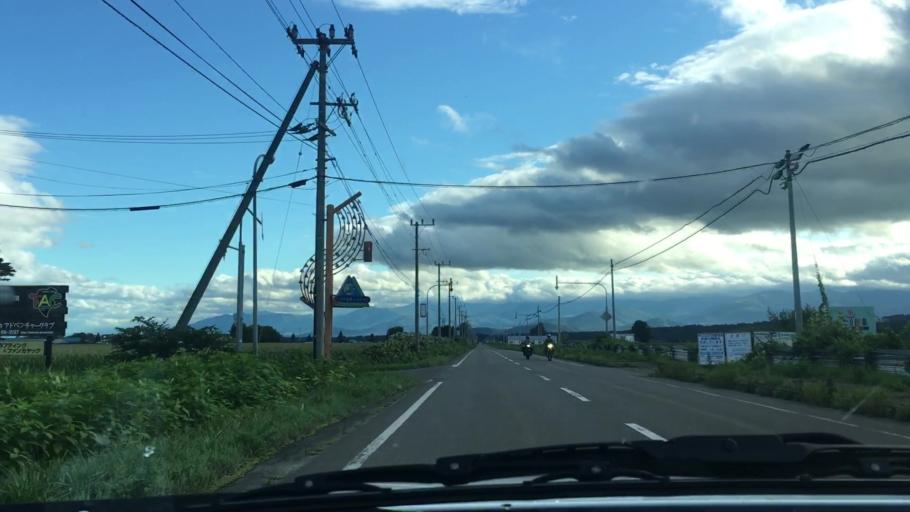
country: JP
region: Hokkaido
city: Otofuke
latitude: 43.1586
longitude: 142.9034
